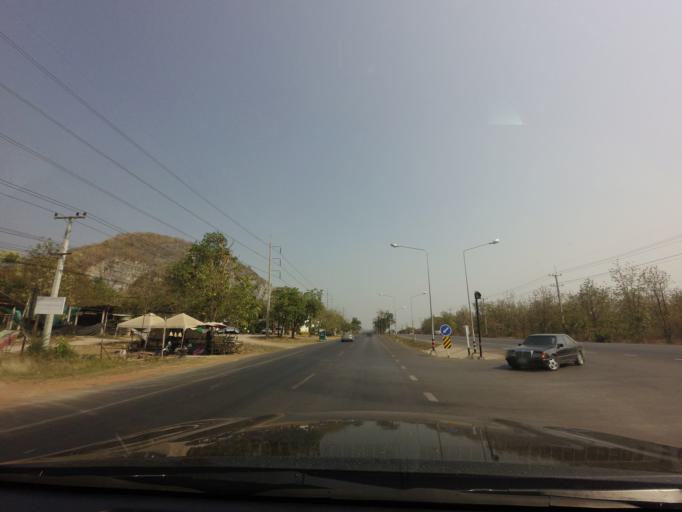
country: TH
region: Kanchanaburi
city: Kanchanaburi
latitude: 14.0617
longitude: 99.5031
